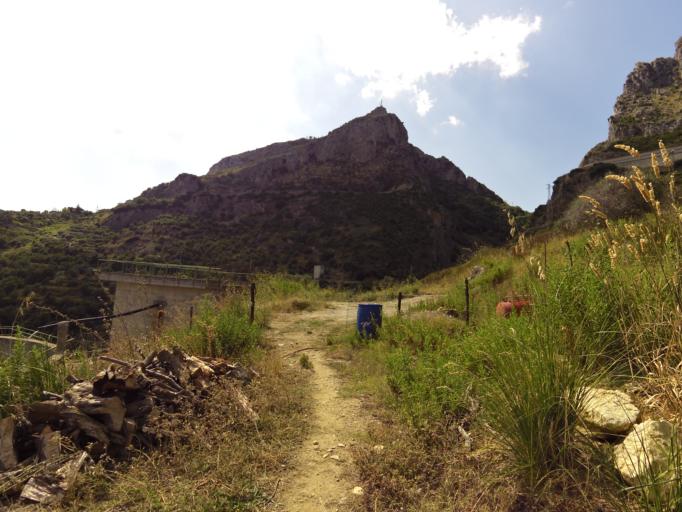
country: IT
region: Calabria
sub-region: Provincia di Reggio Calabria
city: Stilo
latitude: 38.4713
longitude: 16.4597
